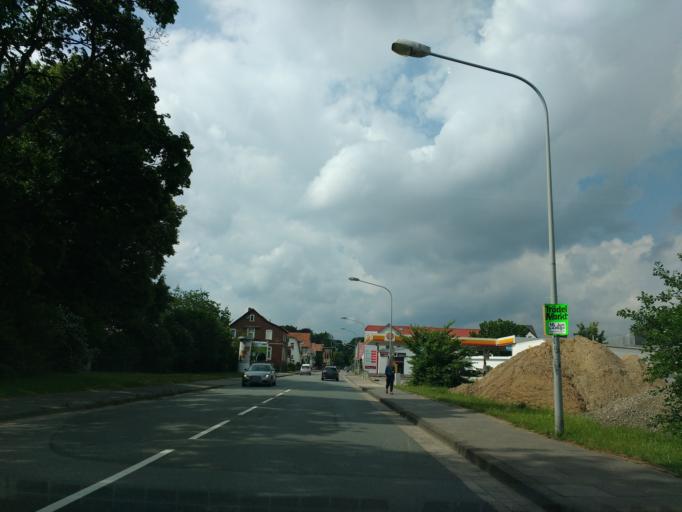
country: DE
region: North Rhine-Westphalia
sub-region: Regierungsbezirk Detmold
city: Lemgo
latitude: 52.0308
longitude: 8.9061
